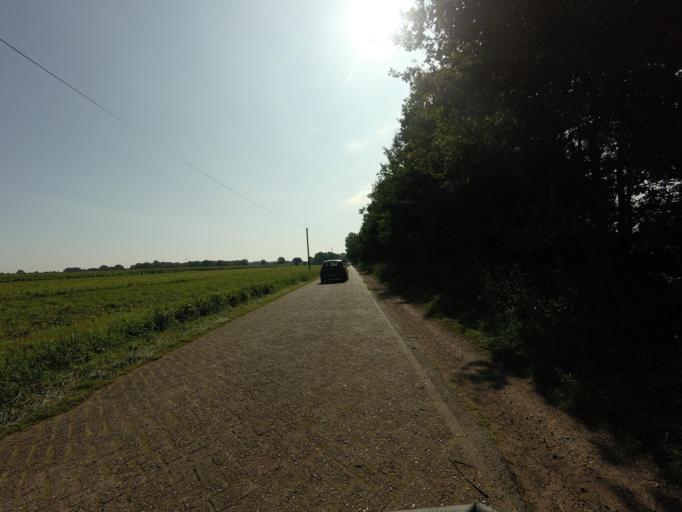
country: DE
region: Lower Saxony
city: Wilsum
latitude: 52.5678
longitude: 6.8241
